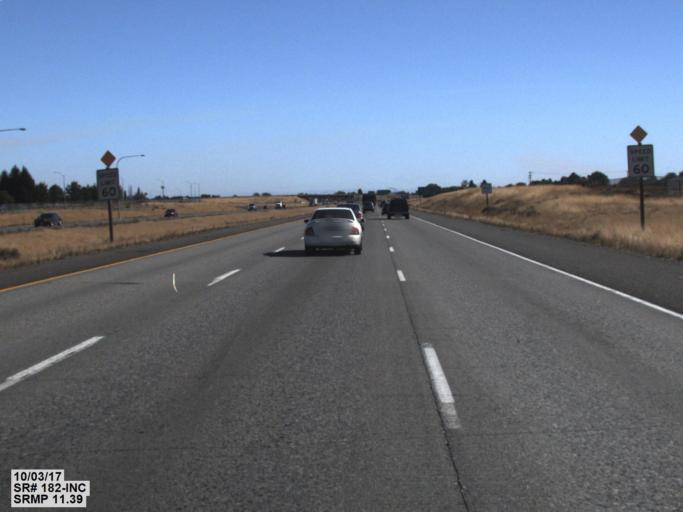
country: US
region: Washington
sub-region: Franklin County
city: West Pasco
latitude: 46.2533
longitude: -119.1430
